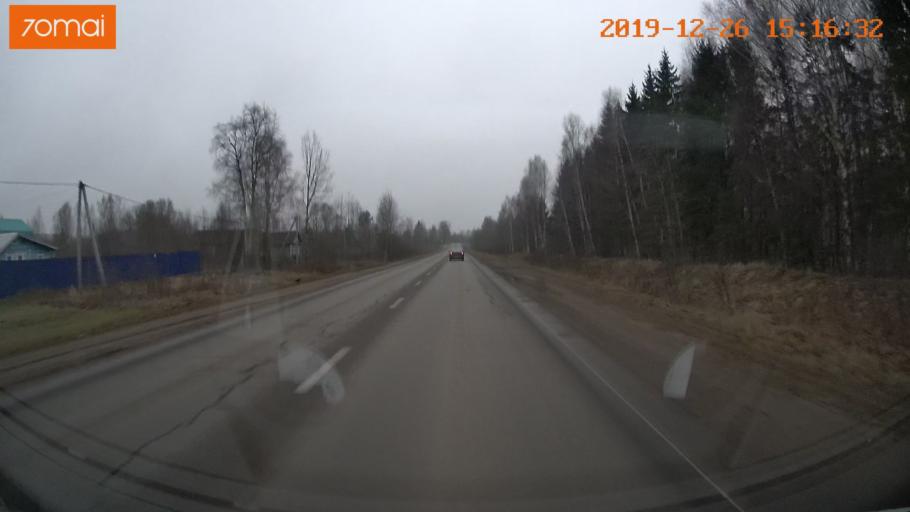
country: RU
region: Jaroslavl
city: Rybinsk
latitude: 58.0853
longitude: 38.8640
